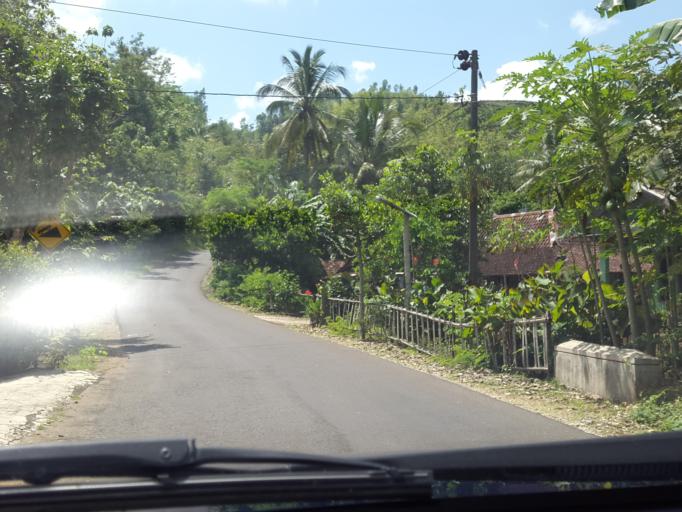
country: ID
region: Daerah Istimewa Yogyakarta
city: Wonosari
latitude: -7.9831
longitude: 110.7356
